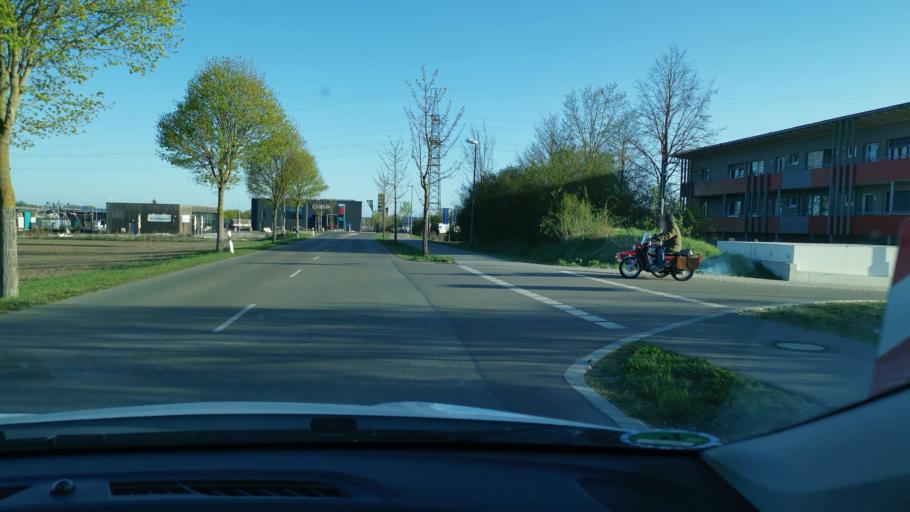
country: DE
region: Bavaria
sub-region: Swabia
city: Meitingen
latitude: 48.5544
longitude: 10.8513
